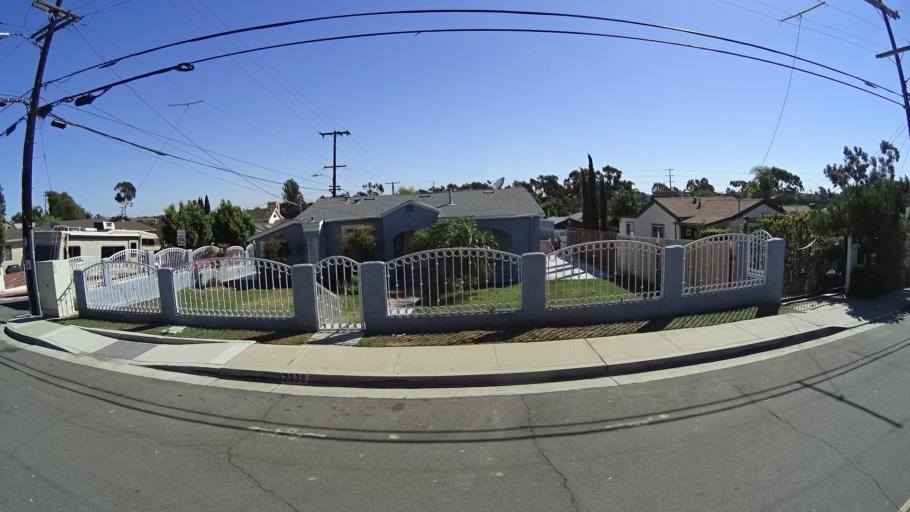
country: US
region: California
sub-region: San Diego County
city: Chula Vista
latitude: 32.6620
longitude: -117.0745
